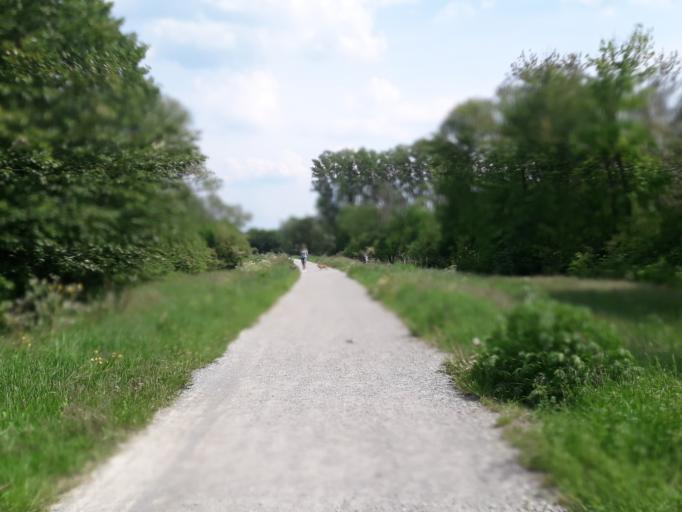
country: DE
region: North Rhine-Westphalia
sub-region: Regierungsbezirk Detmold
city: Paderborn
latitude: 51.7573
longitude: 8.7547
